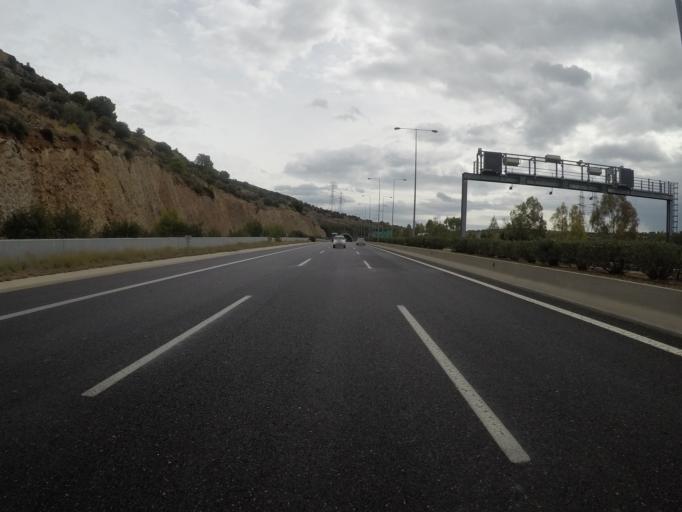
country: GR
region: Attica
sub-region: Nomarchia Dytikis Attikis
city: Fyli
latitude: 38.0840
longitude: 23.6650
